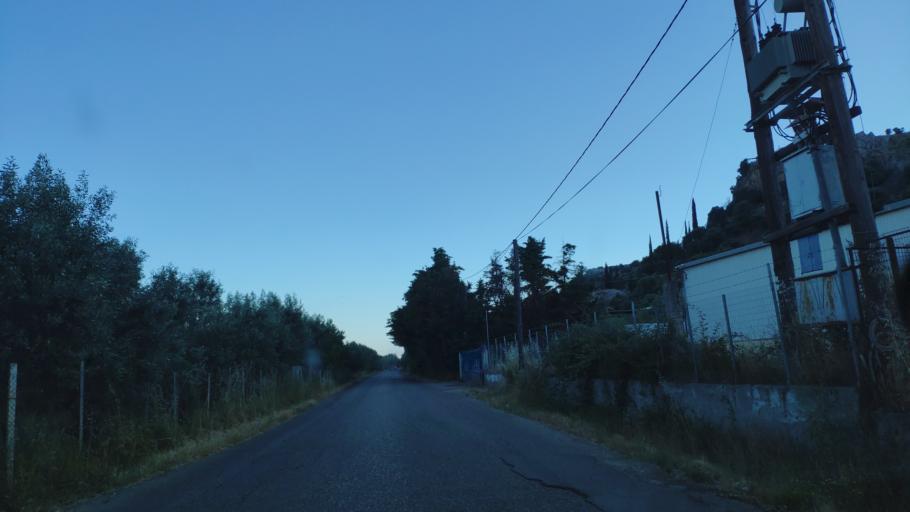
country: GR
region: West Greece
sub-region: Nomos Aitolias kai Akarnanias
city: Astakos
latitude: 38.5525
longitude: 21.0950
